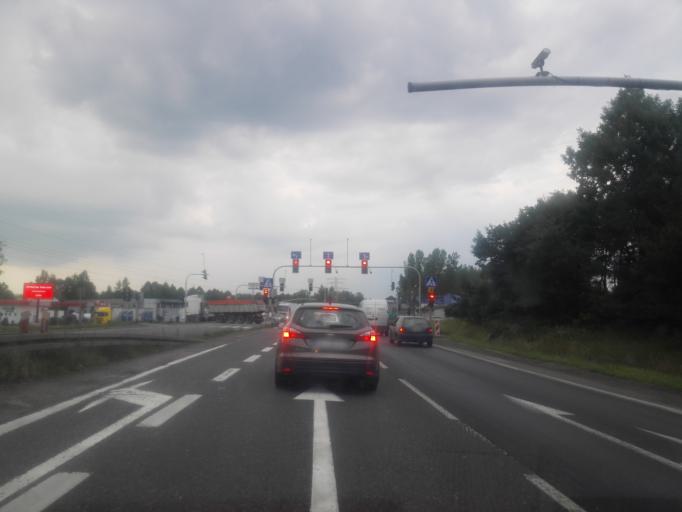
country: PL
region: Silesian Voivodeship
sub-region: Powiat czestochowski
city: Kamienica Polska
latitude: 50.6699
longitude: 19.1226
